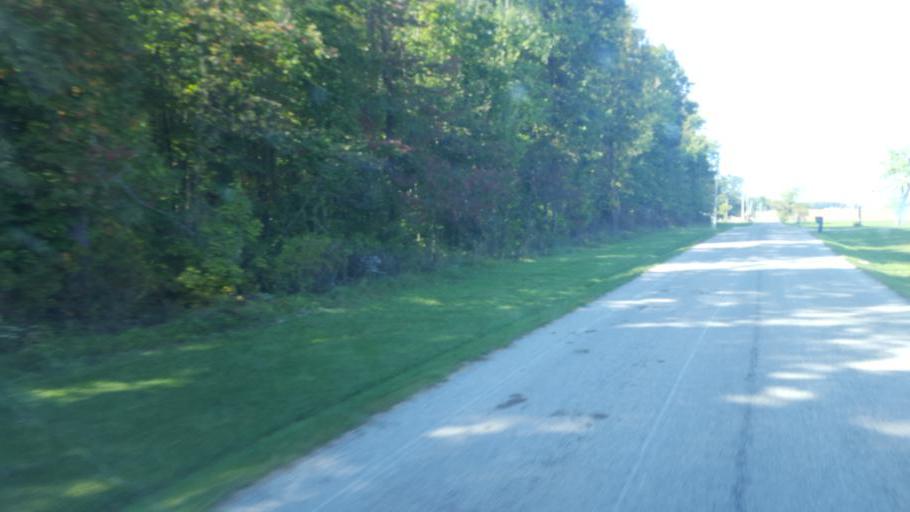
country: US
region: Ohio
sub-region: Morrow County
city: Mount Gilead
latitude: 40.5882
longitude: -82.7000
